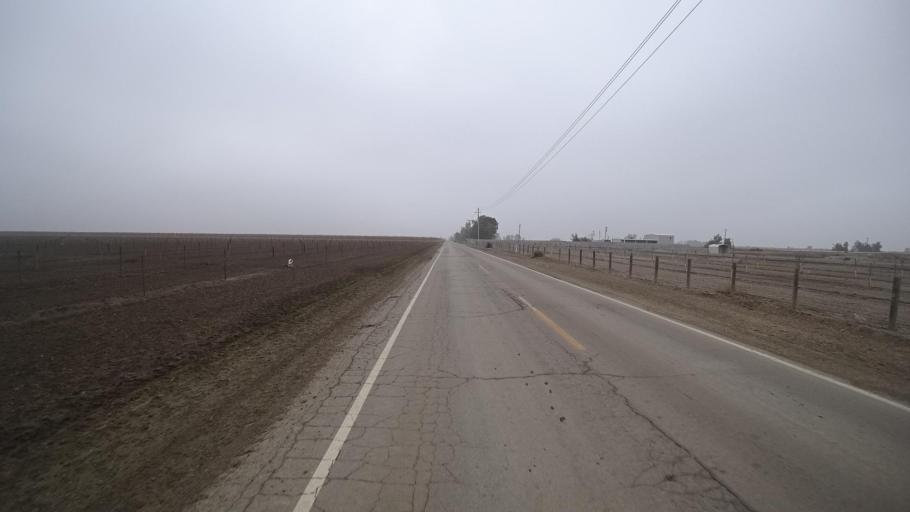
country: US
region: California
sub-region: Tulare County
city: Alpaugh
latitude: 35.6975
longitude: -119.5086
